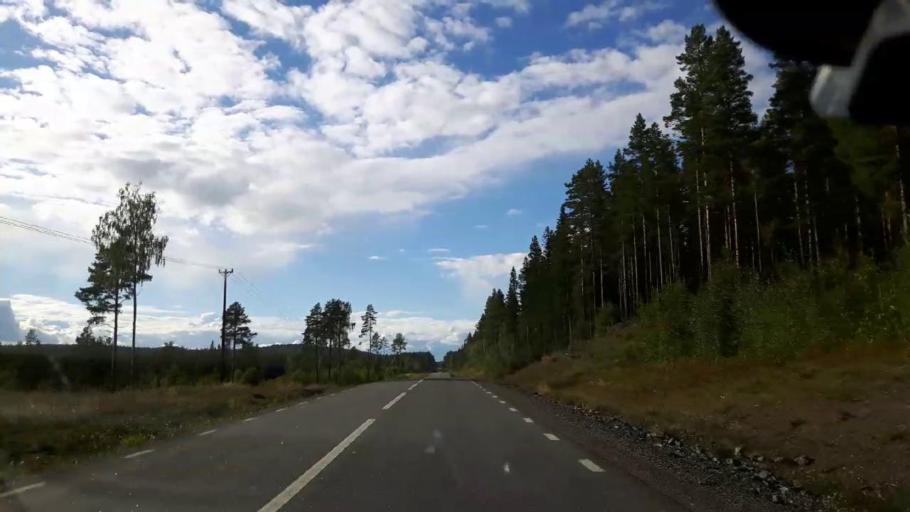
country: SE
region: Jaemtland
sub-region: Stroemsunds Kommun
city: Stroemsund
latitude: 63.5569
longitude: 15.8208
